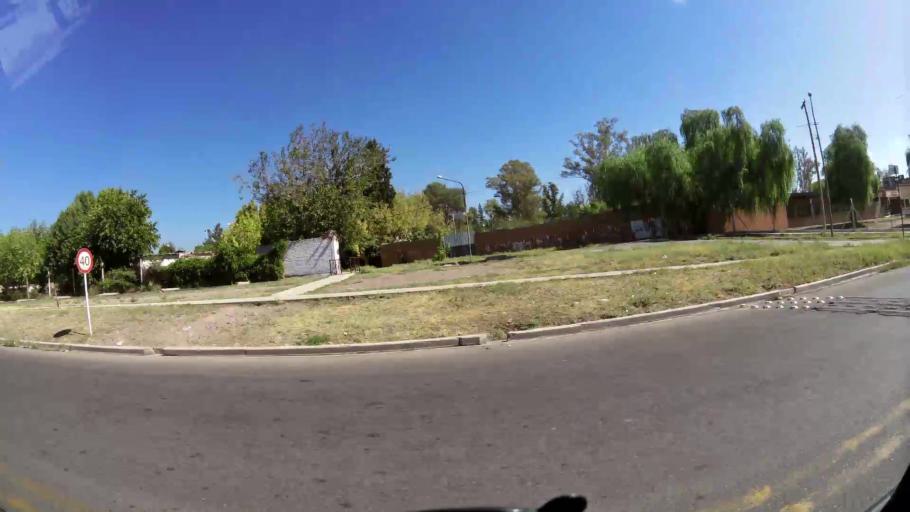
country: AR
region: Mendoza
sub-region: Departamento de Godoy Cruz
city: Godoy Cruz
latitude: -32.9052
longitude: -68.8690
